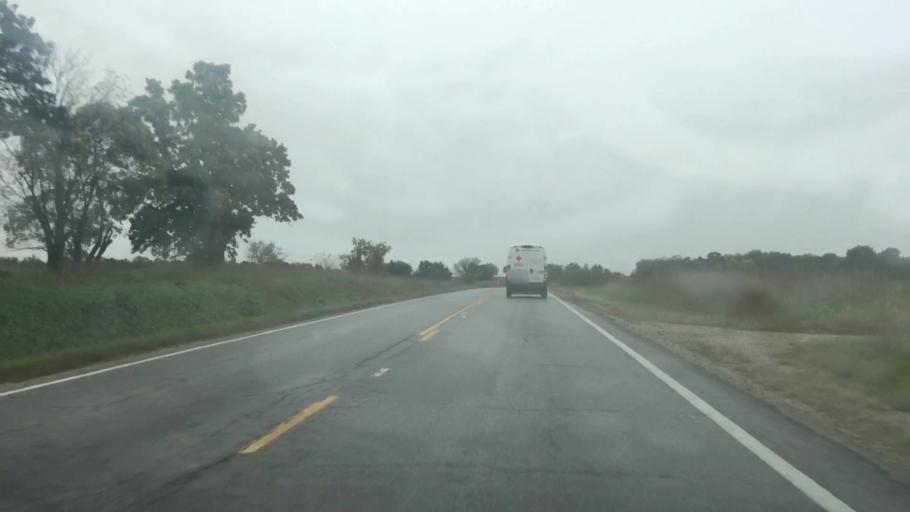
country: US
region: Kansas
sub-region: Anderson County
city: Garnett
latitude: 38.2458
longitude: -95.2483
